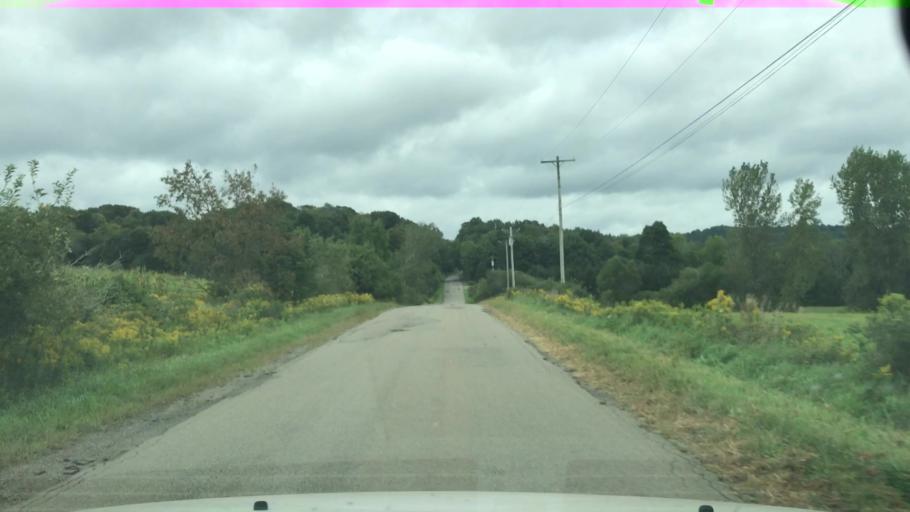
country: US
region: New York
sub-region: Cattaraugus County
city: Little Valley
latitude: 42.3293
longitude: -78.7244
